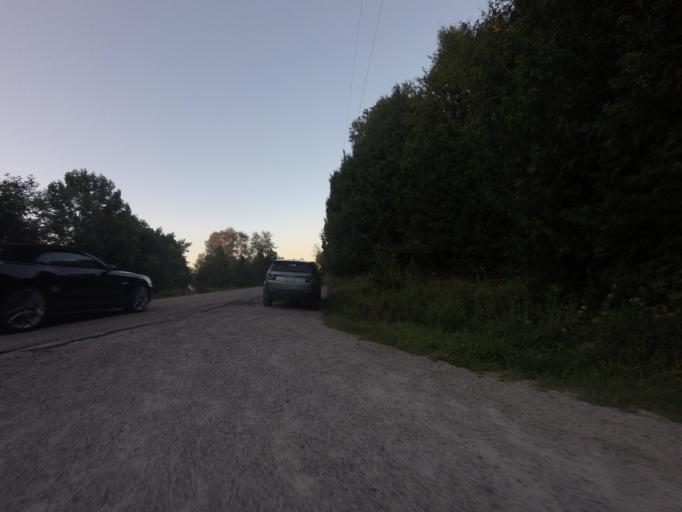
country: CA
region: Ontario
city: Orangeville
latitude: 43.9344
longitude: -79.8435
